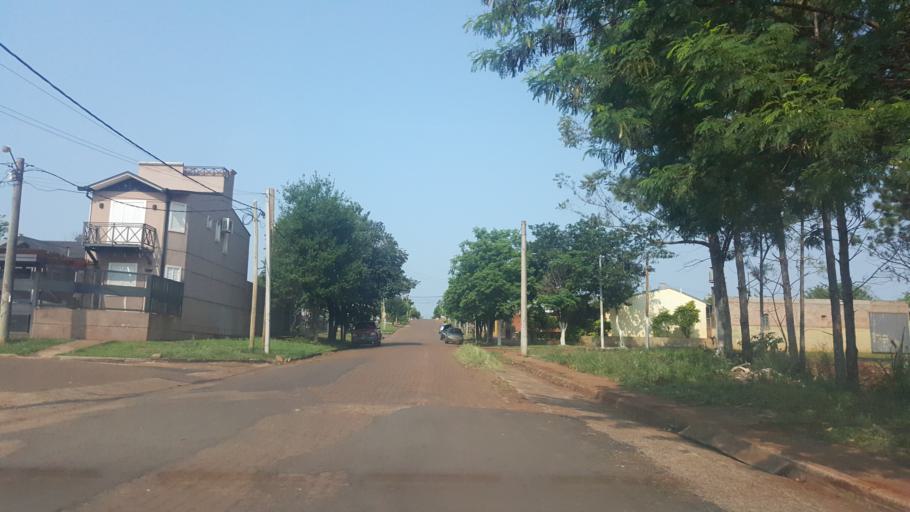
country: AR
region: Misiones
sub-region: Departamento de Capital
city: Posadas
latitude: -27.4172
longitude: -55.9559
